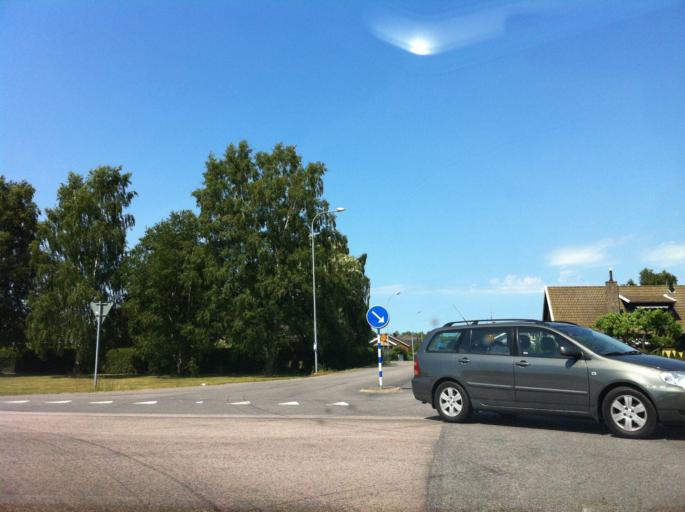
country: SE
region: Skane
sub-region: Bjuvs Kommun
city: Bjuv
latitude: 56.0765
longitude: 12.9098
